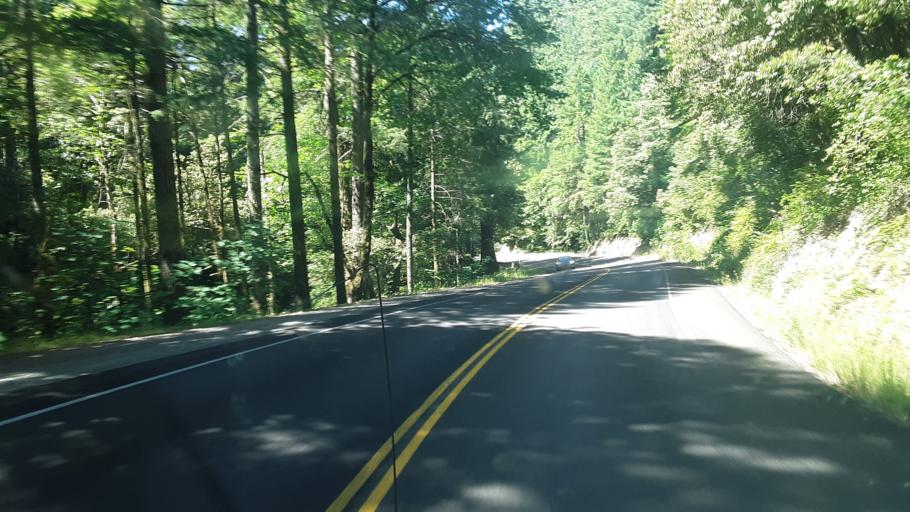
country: US
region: Oregon
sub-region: Josephine County
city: Cave Junction
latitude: 41.9282
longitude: -123.7576
